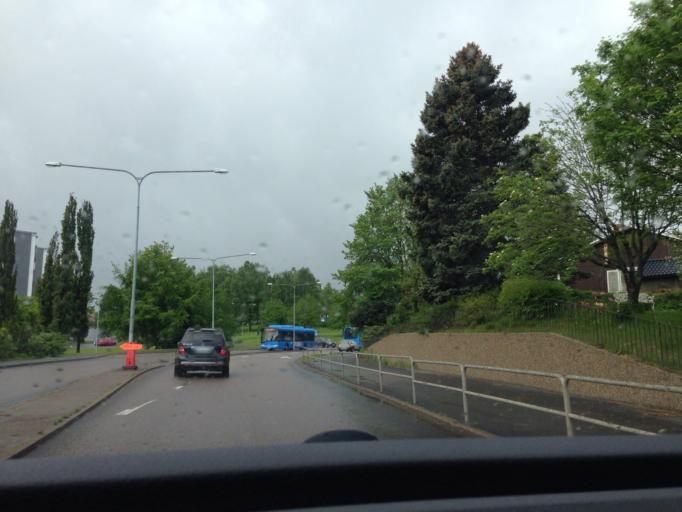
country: SE
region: Vaestra Goetaland
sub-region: Skovde Kommun
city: Skoevde
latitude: 58.3923
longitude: 13.8654
